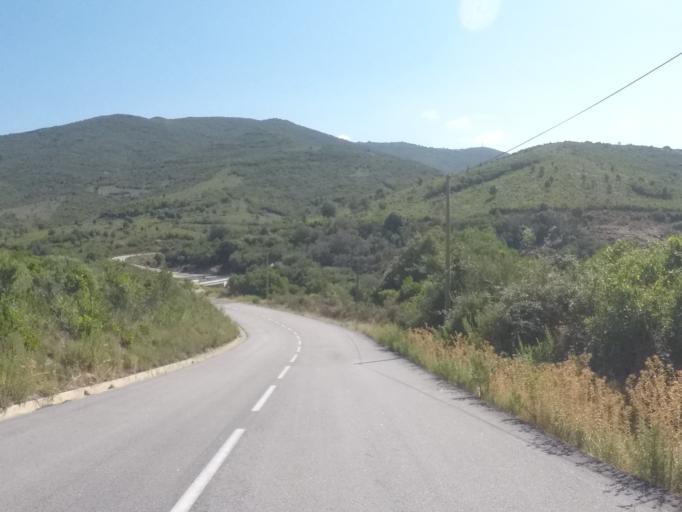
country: FR
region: Corsica
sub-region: Departement de la Haute-Corse
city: Calvi
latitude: 42.4305
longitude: 8.7322
